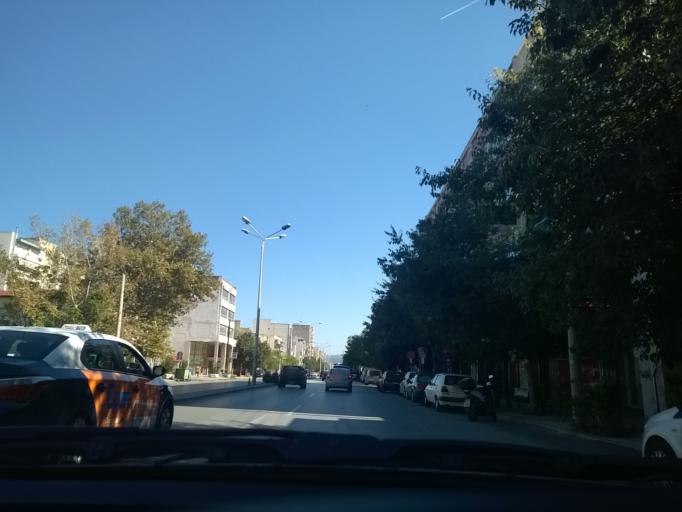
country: GR
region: Central Macedonia
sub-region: Nomos Thessalonikis
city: Ampelokipoi
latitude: 40.6492
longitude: 22.9185
